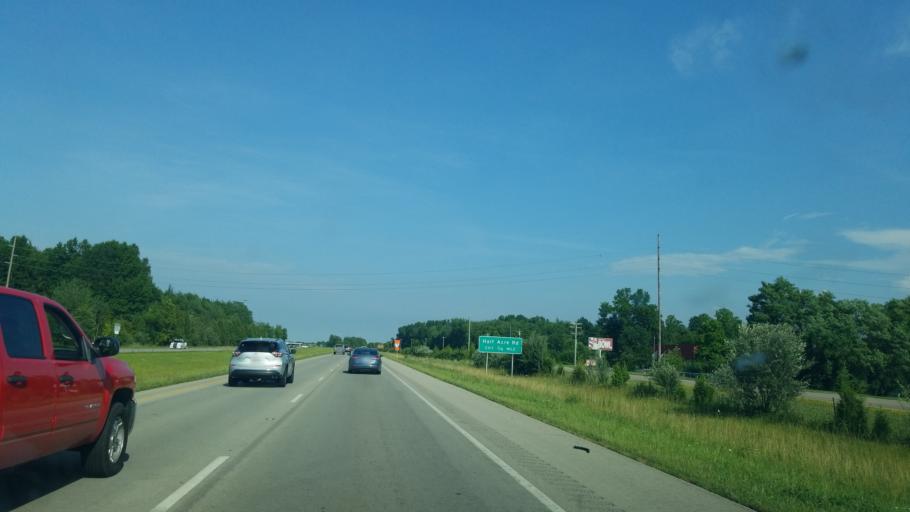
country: US
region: Ohio
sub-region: Clermont County
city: Williamsburg
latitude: 39.0730
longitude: -84.1107
